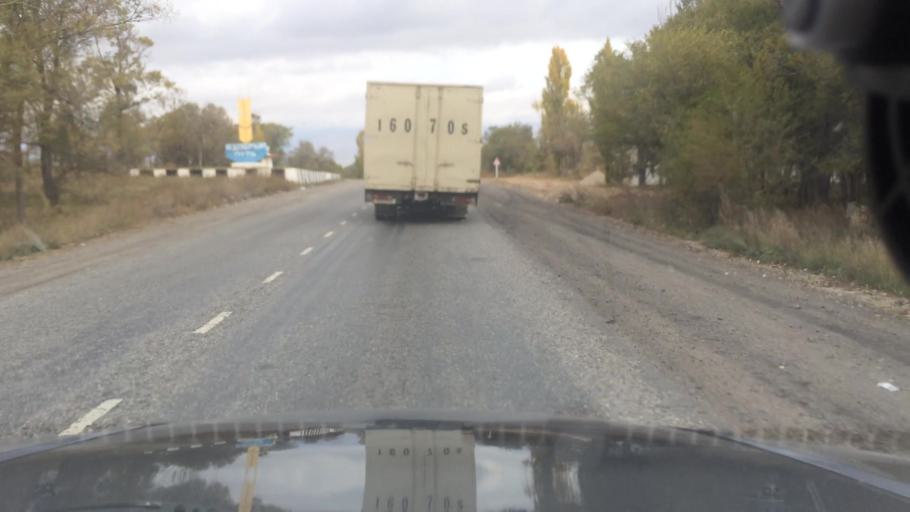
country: KG
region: Ysyk-Koel
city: Tyup
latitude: 42.6655
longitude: 78.3495
